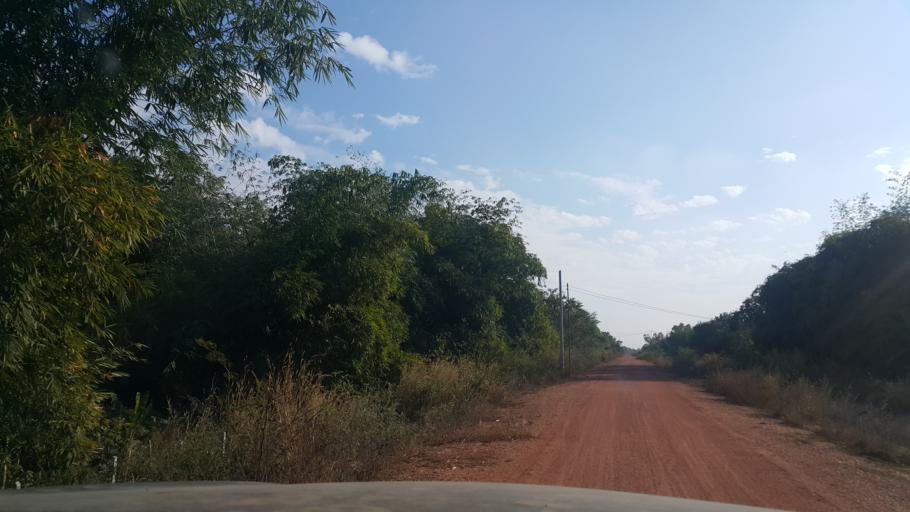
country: TH
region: Lampang
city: Hang Chat
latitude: 18.2747
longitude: 99.3722
